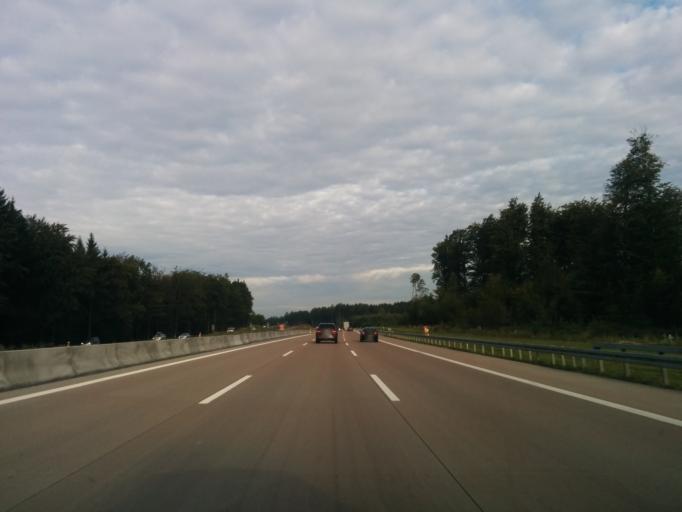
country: DE
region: Bavaria
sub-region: Swabia
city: Zusmarshausen
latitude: 48.4098
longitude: 10.6282
